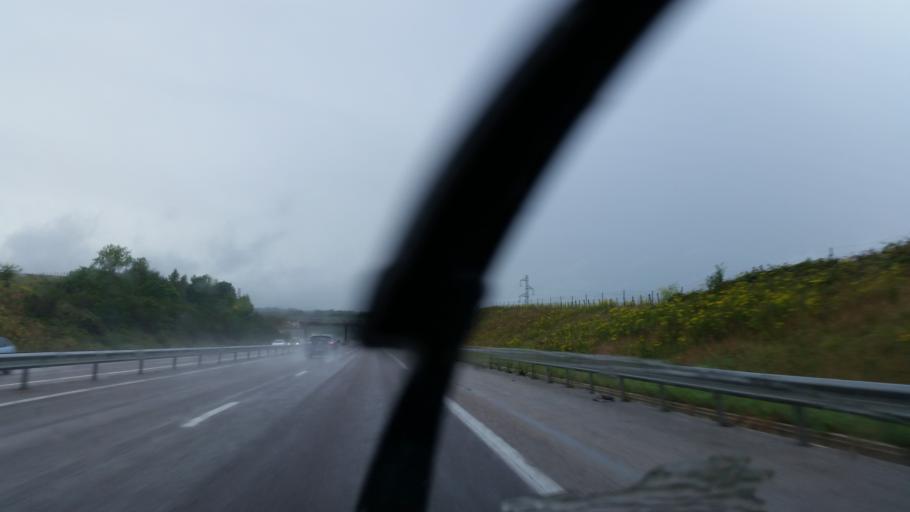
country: FR
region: Franche-Comte
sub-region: Departement de la Haute-Saone
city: Hericourt
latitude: 47.5909
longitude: 6.7323
